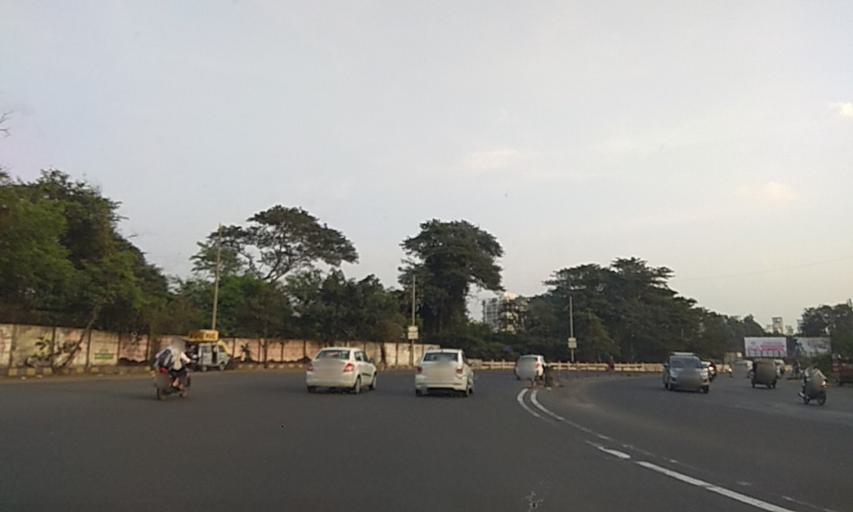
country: IN
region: Maharashtra
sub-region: Pune Division
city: Khadki
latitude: 18.5693
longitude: 73.8111
